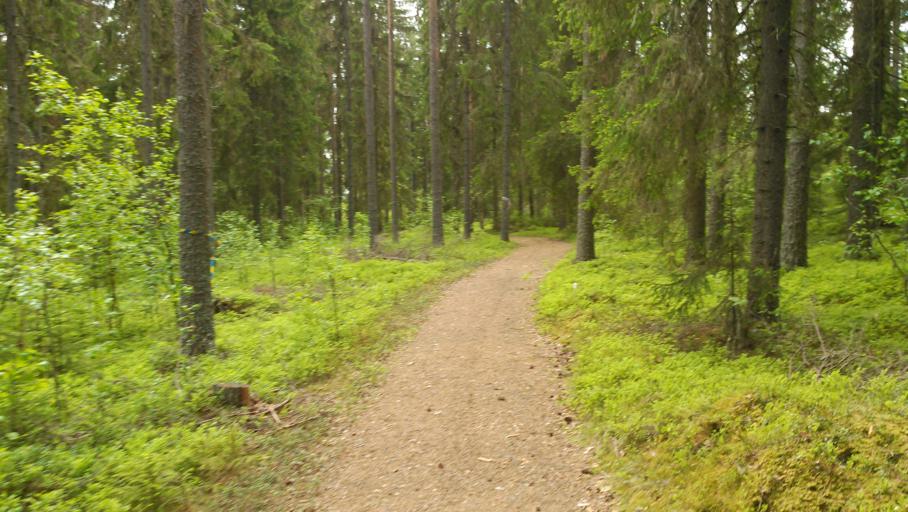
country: SE
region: Vaesterbotten
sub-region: Vannas Kommun
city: Vannasby
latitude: 64.0170
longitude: 19.9018
